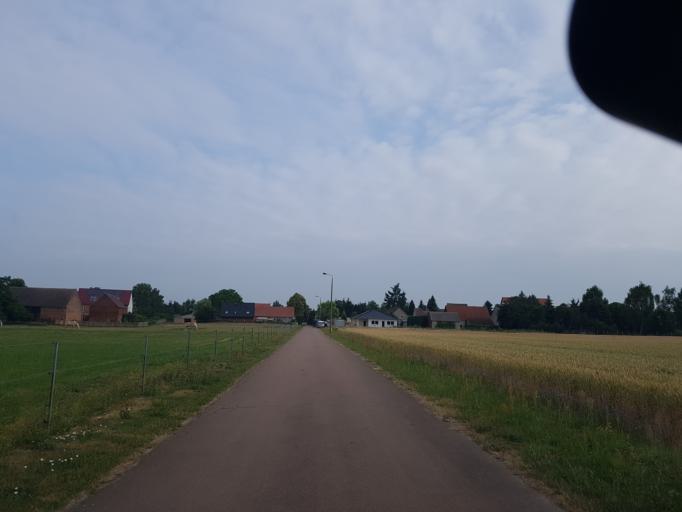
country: DE
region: Brandenburg
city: Niedergorsdorf
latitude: 51.9526
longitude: 12.9191
